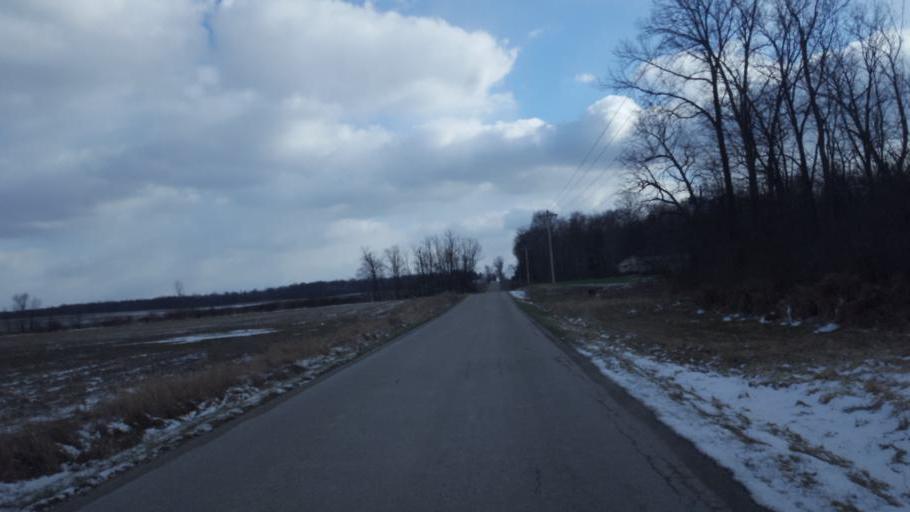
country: US
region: Ohio
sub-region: Morrow County
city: Mount Gilead
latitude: 40.6204
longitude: -82.7283
